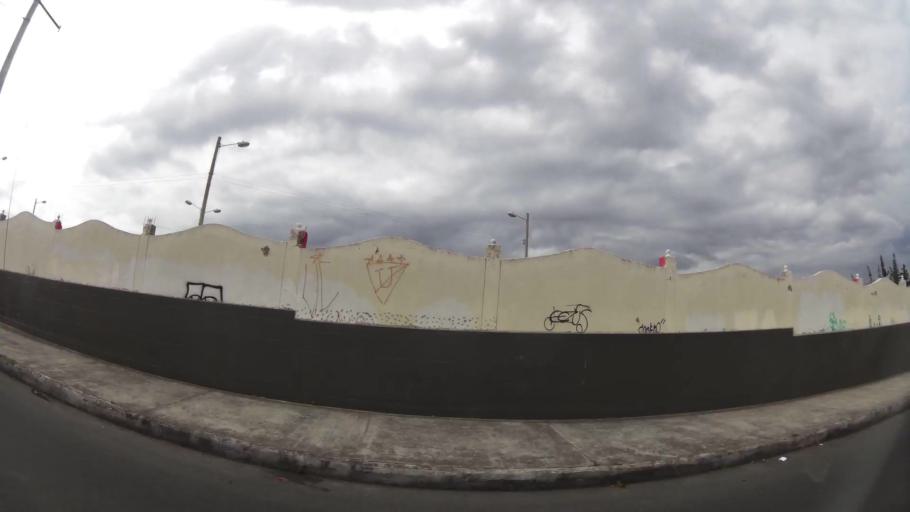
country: EC
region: Tungurahua
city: Ambato
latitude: -1.2709
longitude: -78.6232
